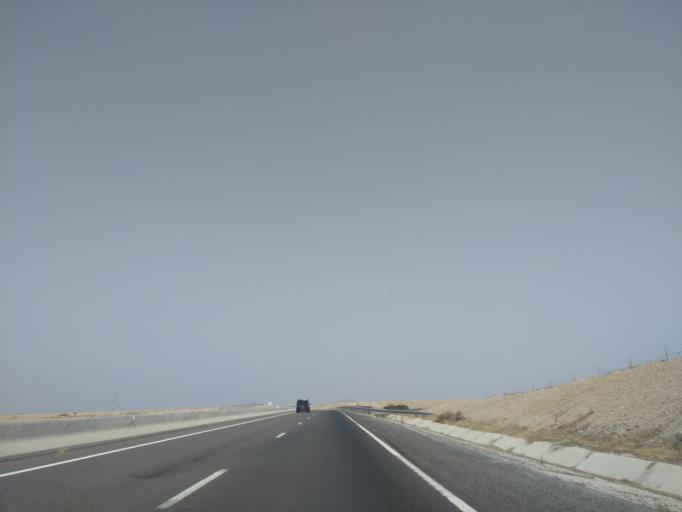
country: MA
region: Marrakech-Tensift-Al Haouz
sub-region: Chichaoua
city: Chichaoua
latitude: 31.5314
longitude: -8.4871
